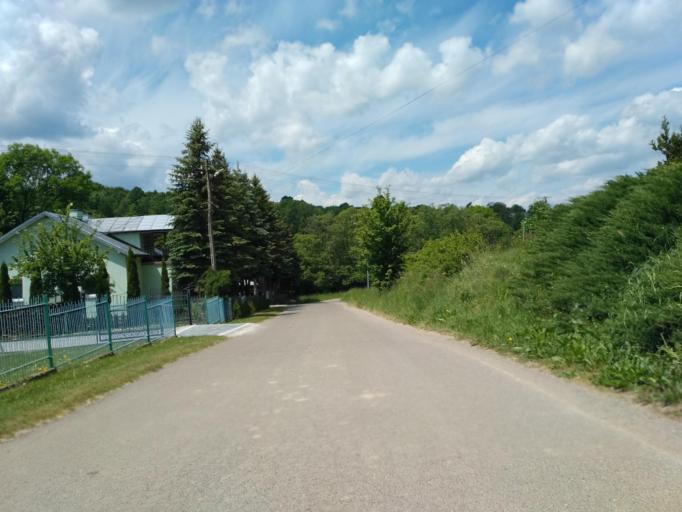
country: PL
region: Subcarpathian Voivodeship
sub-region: Powiat krosnienski
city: Dukla
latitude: 49.5848
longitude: 21.6236
